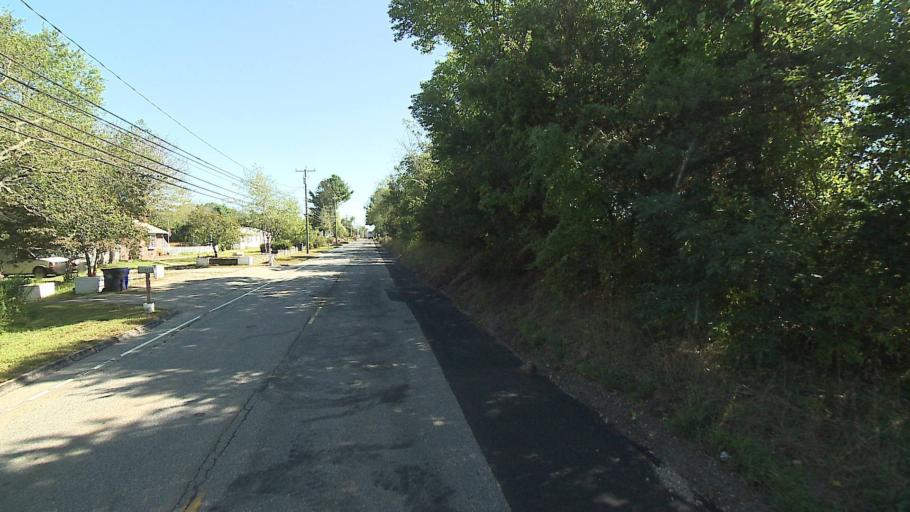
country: US
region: Connecticut
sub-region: New London County
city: Jewett City
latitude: 41.6391
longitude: -71.9498
